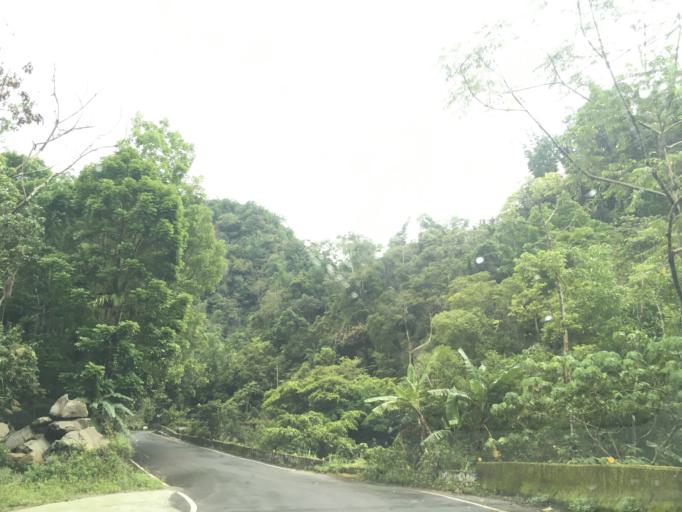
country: TW
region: Taiwan
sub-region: Yunlin
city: Douliu
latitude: 23.5643
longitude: 120.6407
